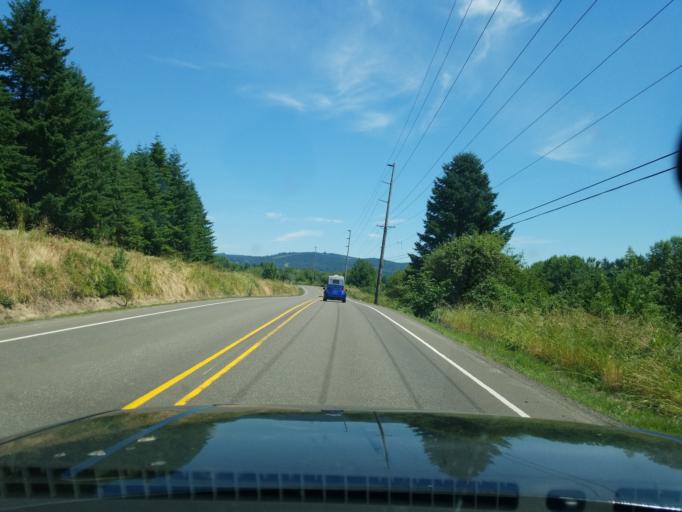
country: US
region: Oregon
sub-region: Yamhill County
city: Yamhill
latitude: 45.3995
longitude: -123.1265
